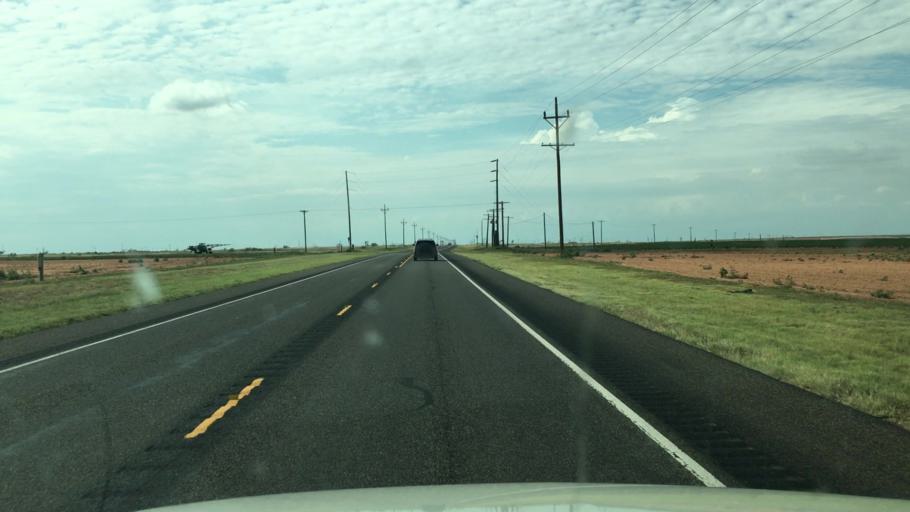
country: US
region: Texas
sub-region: Dawson County
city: Lamesa
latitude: 32.8884
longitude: -102.0881
